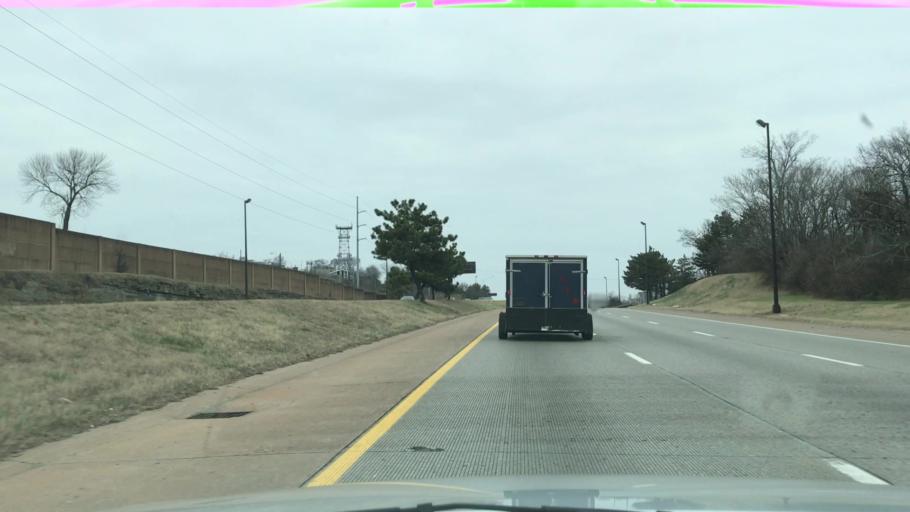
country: US
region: Tennessee
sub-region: Davidson County
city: Nashville
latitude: 36.1500
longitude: -86.8225
